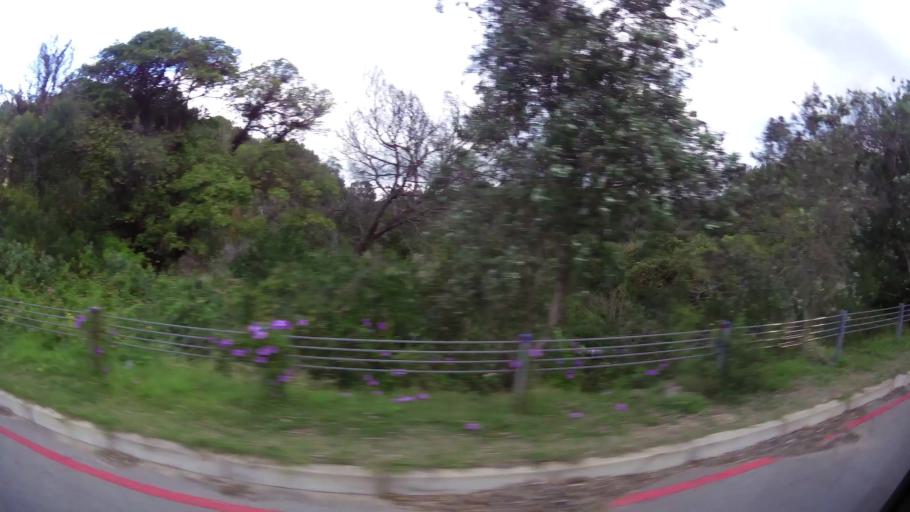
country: ZA
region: Western Cape
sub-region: Eden District Municipality
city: Plettenberg Bay
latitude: -34.0496
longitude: 23.3714
